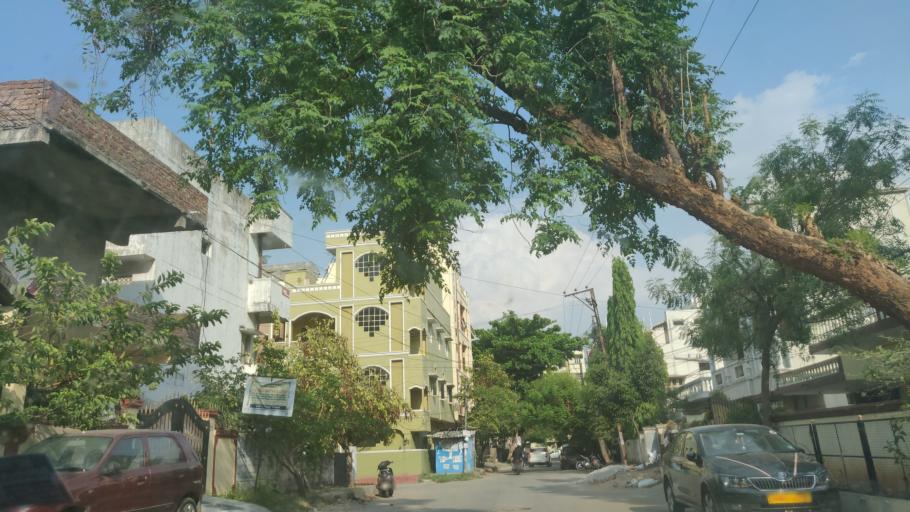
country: IN
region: Telangana
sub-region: Rangareddi
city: Gaddi Annaram
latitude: 17.3746
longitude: 78.5201
